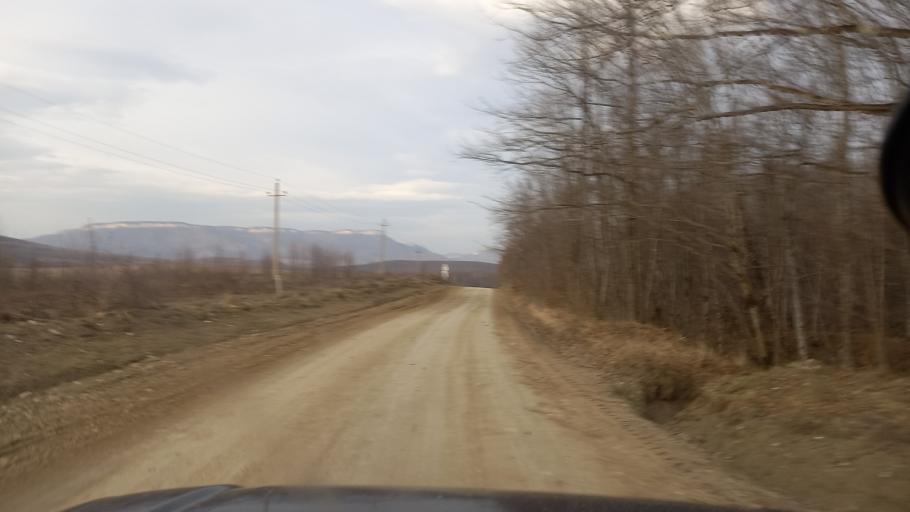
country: RU
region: Adygeya
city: Kamennomostskiy
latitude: 44.1559
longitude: 40.2420
